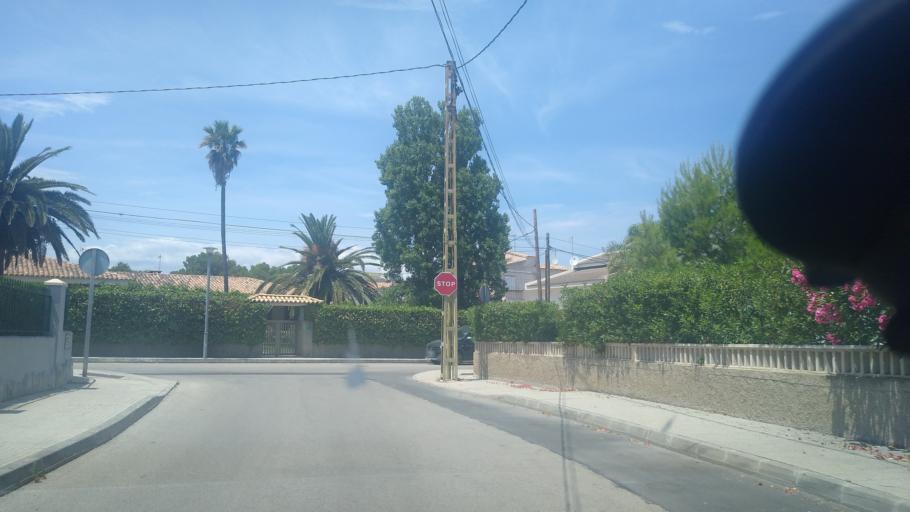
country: ES
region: Balearic Islands
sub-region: Illes Balears
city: Santa Margalida
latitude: 39.7589
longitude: 3.1644
